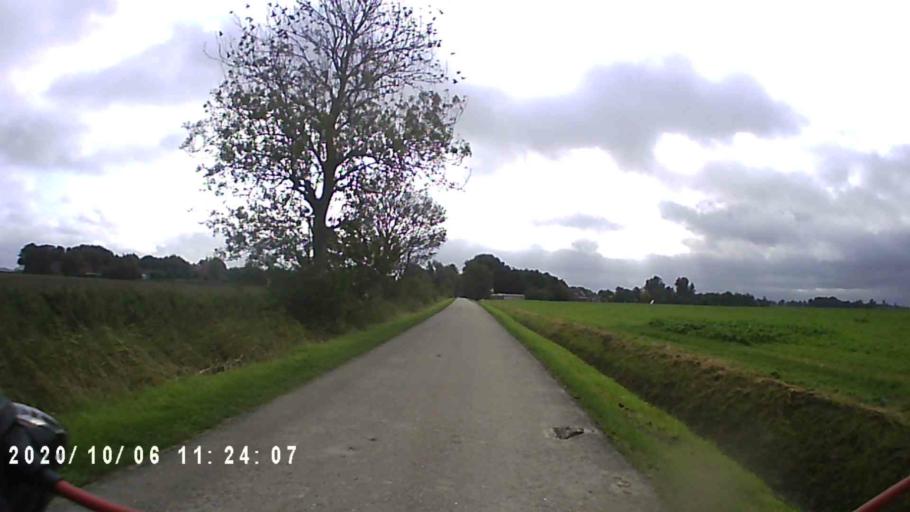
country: NL
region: Groningen
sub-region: Gemeente Zuidhorn
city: Oldehove
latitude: 53.3433
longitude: 6.4185
